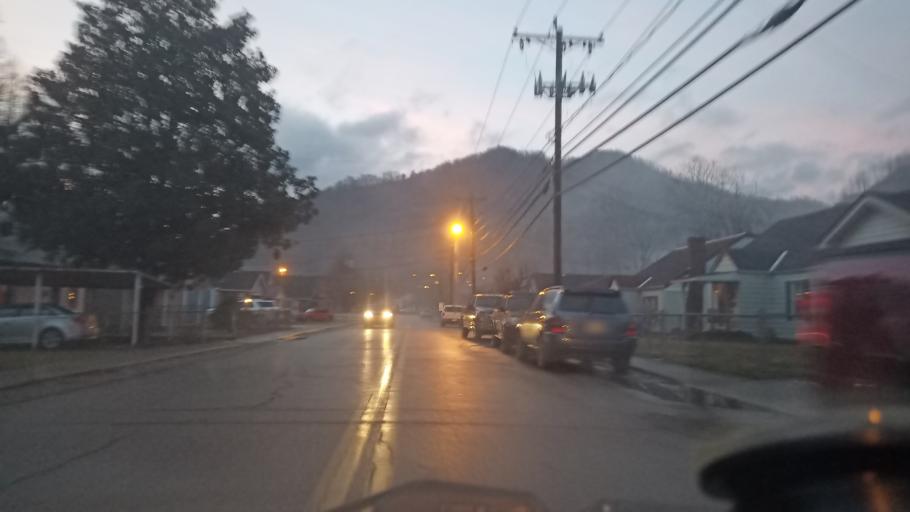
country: US
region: West Virginia
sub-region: Logan County
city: Mallory
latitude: 37.7368
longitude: -81.8758
